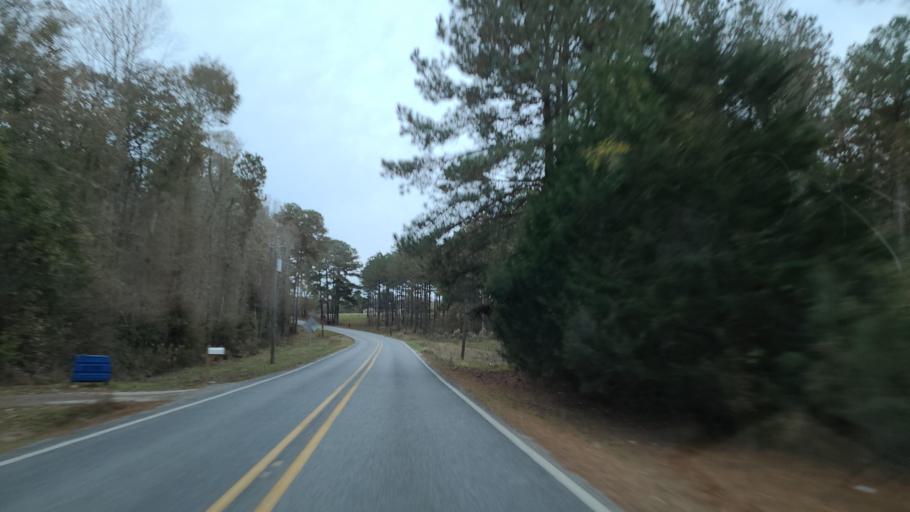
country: US
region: Mississippi
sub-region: Clarke County
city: Quitman
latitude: 32.0291
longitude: -88.8189
